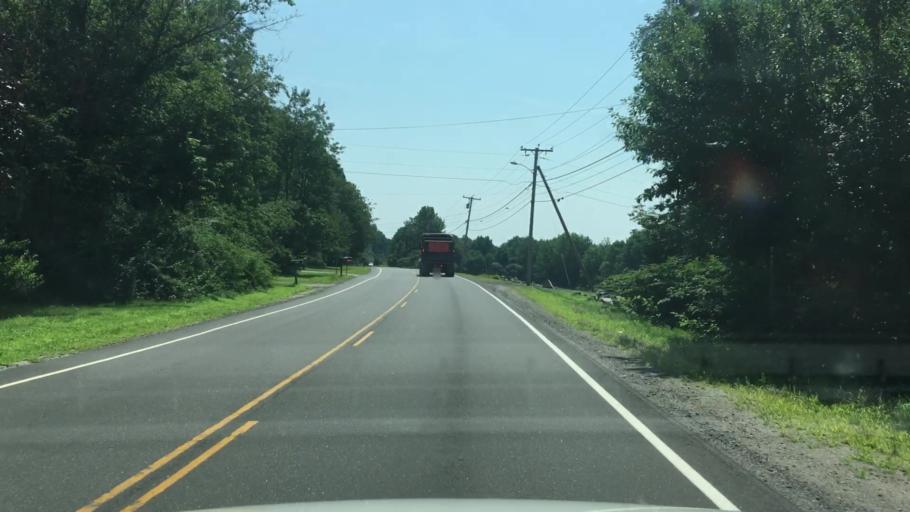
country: US
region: Maine
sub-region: Kennebec County
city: Manchester
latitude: 44.3076
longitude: -69.8255
